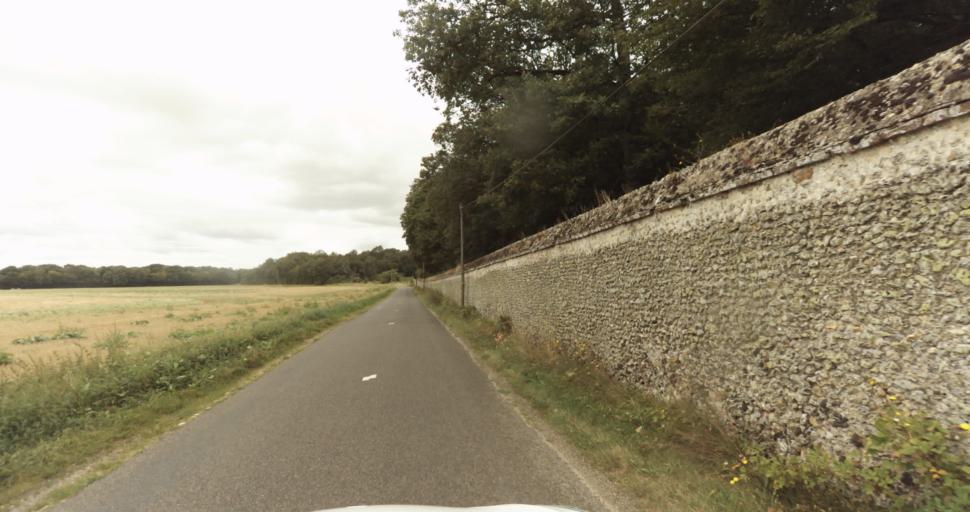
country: FR
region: Centre
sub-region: Departement d'Eure-et-Loir
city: Saint-Lubin-des-Joncherets
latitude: 48.8213
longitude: 1.2344
